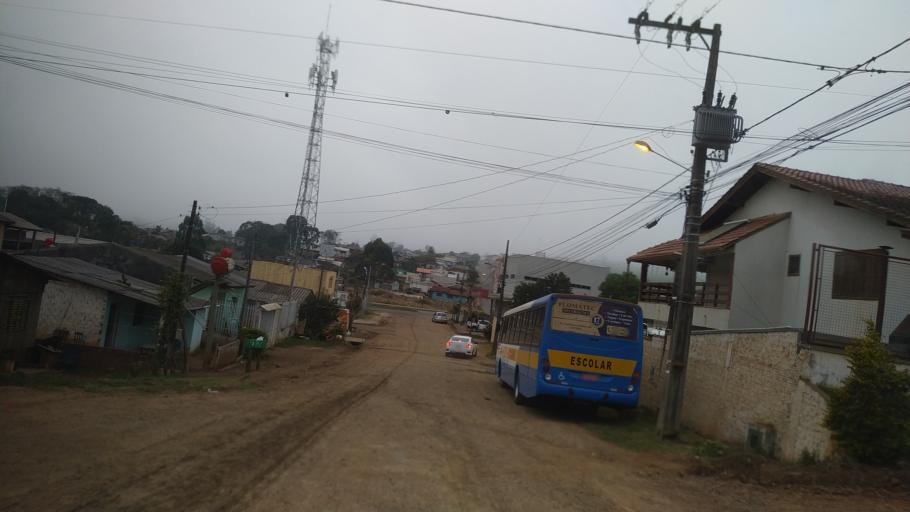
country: BR
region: Santa Catarina
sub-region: Chapeco
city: Chapeco
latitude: -27.1315
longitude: -52.6038
